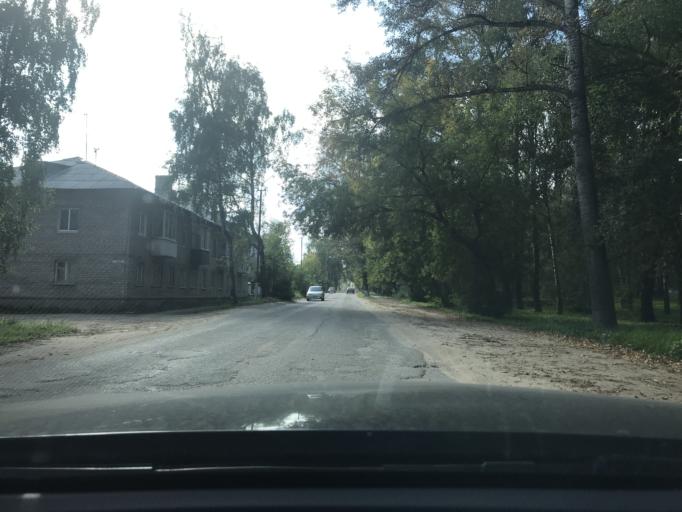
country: RU
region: Tverskaya
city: Bezhetsk
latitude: 57.7874
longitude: 36.6985
